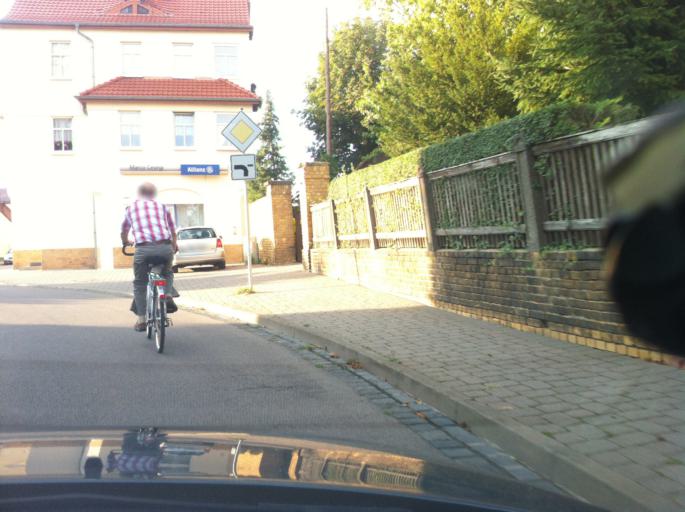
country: DE
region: Saxony
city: Markkleeberg
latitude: 51.2753
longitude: 12.3117
